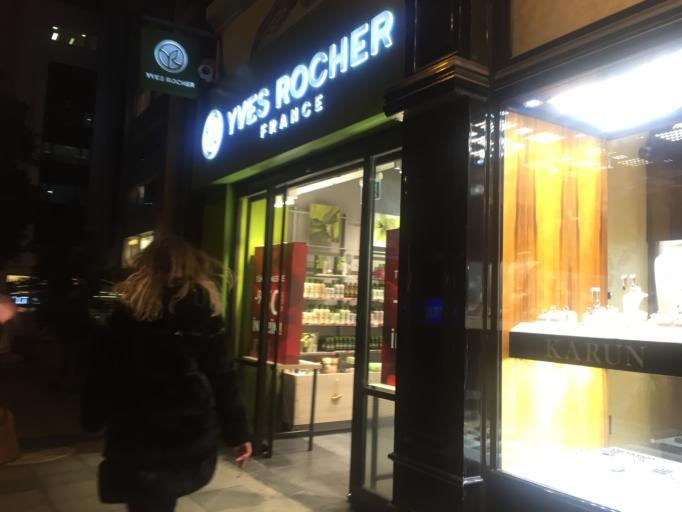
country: TR
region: Istanbul
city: Sisli
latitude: 41.0499
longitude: 28.9934
